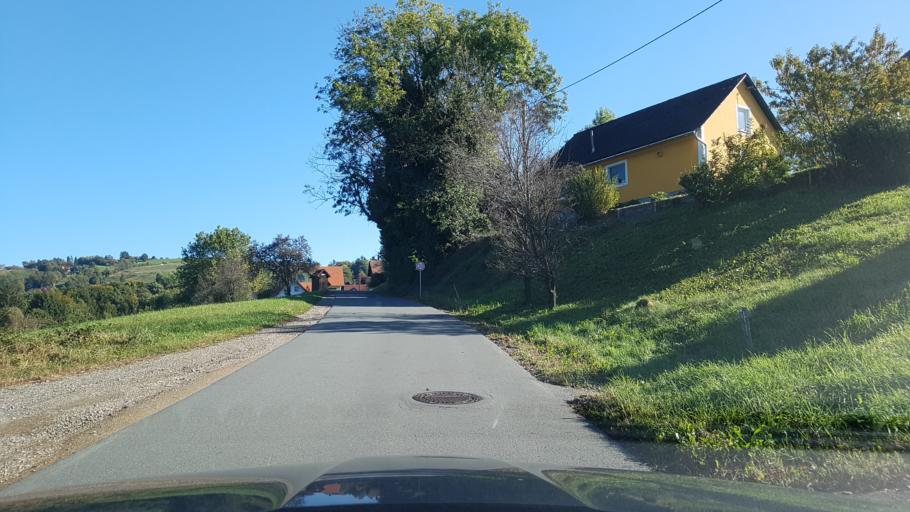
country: AT
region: Styria
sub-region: Politischer Bezirk Leibnitz
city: Kitzeck im Sausal
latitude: 46.7719
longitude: 15.4148
